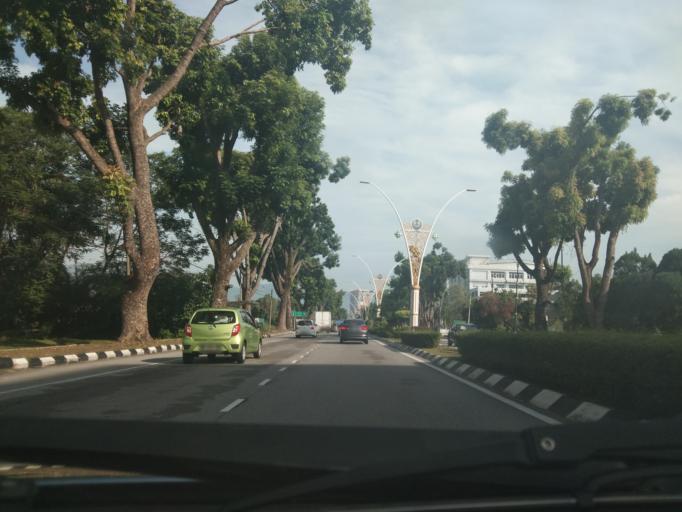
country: MY
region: Perak
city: Ipoh
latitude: 4.5894
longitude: 101.0941
